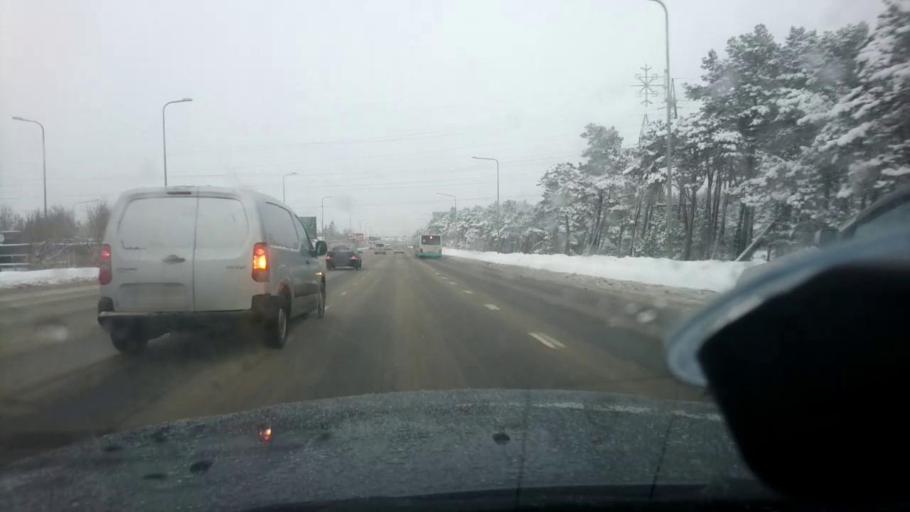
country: EE
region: Harju
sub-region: Tallinna linn
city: Tallinn
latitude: 59.3954
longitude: 24.7254
